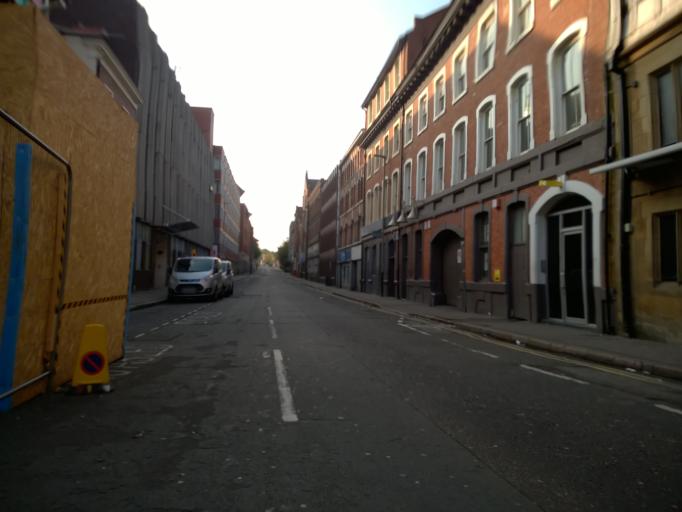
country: GB
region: England
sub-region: City of Leicester
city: Leicester
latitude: 52.6318
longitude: -1.1322
